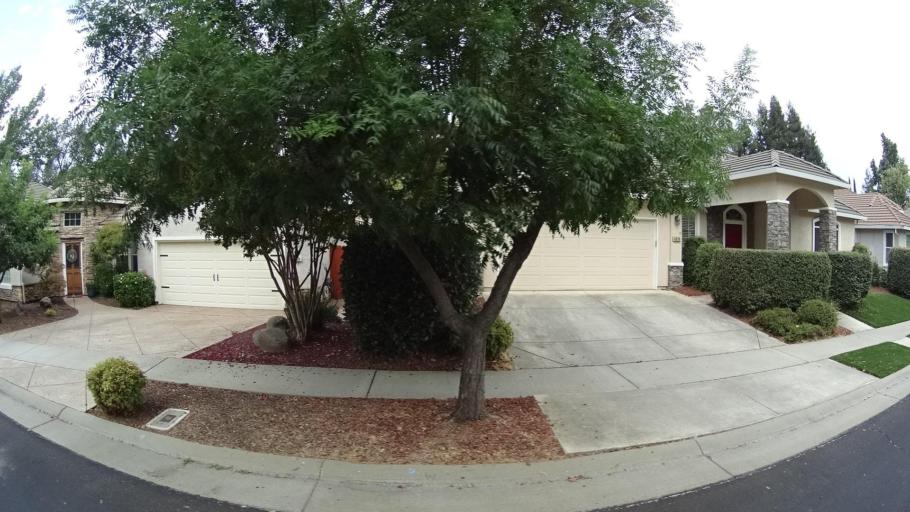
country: US
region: California
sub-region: Placer County
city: Loomis
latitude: 38.8093
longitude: -121.2003
